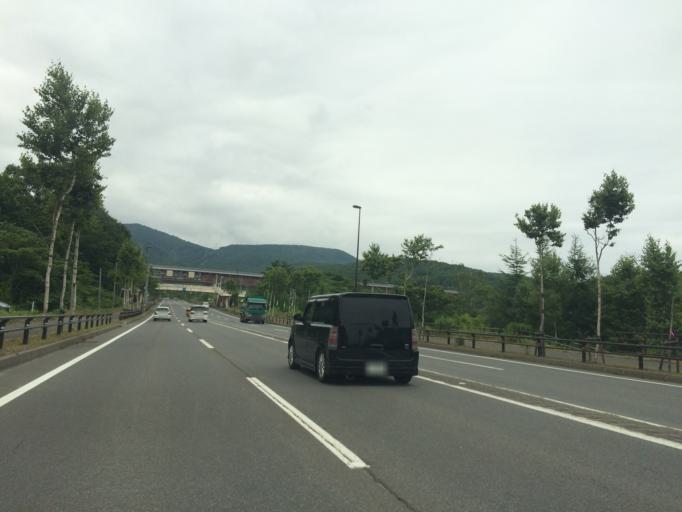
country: JP
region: Hokkaido
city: Otaru
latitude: 43.1531
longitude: 141.1214
